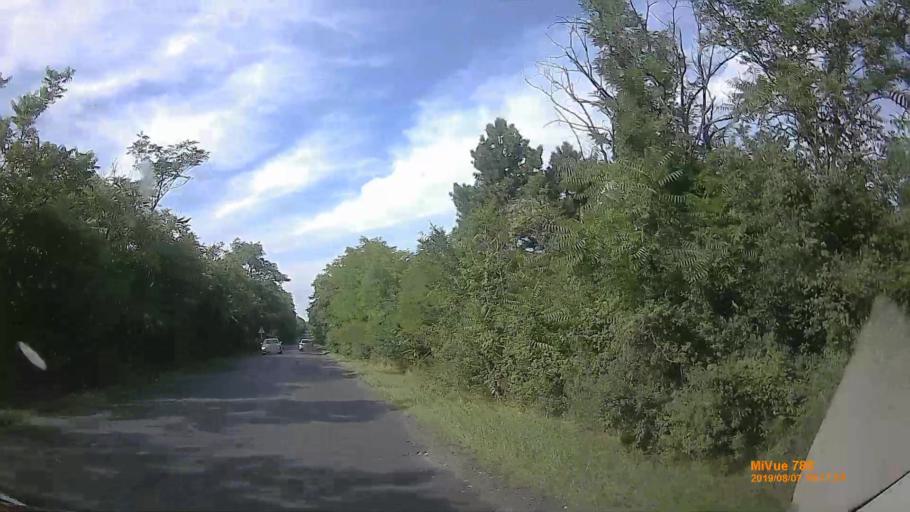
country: HU
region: Zala
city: Cserszegtomaj
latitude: 46.8312
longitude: 17.2708
